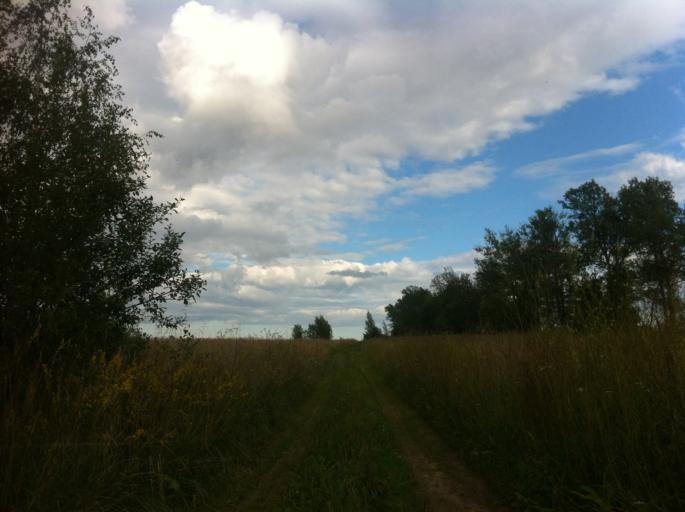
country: RU
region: Pskov
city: Izborsk
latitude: 57.8189
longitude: 27.9725
